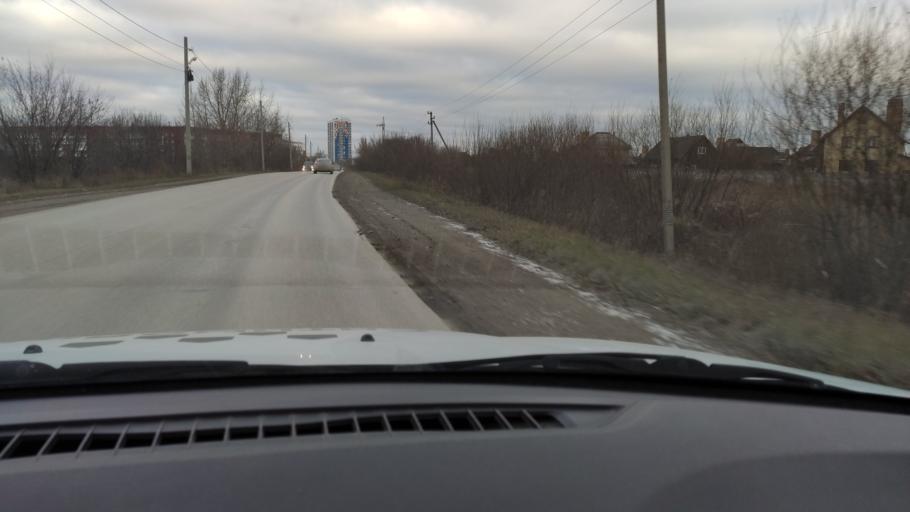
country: RU
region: Perm
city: Kondratovo
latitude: 57.9710
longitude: 56.1151
